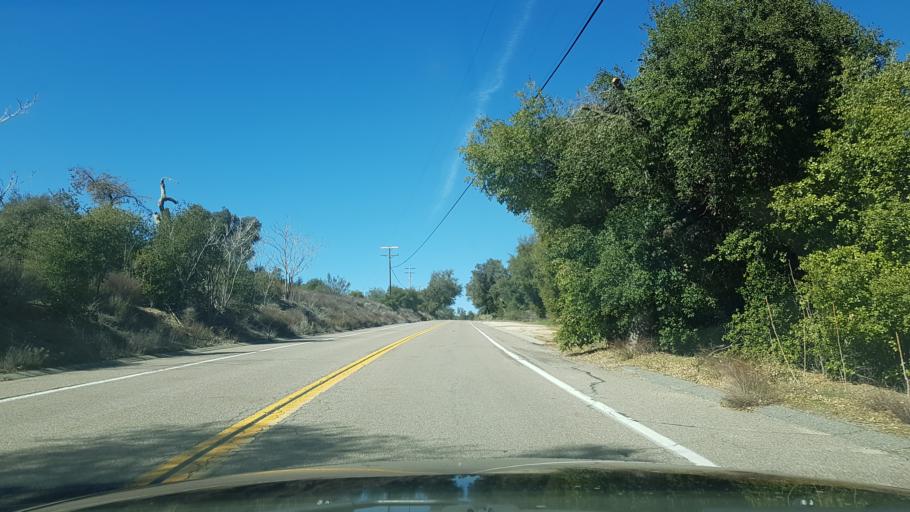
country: US
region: California
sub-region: San Diego County
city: Julian
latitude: 33.2019
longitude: -116.6020
